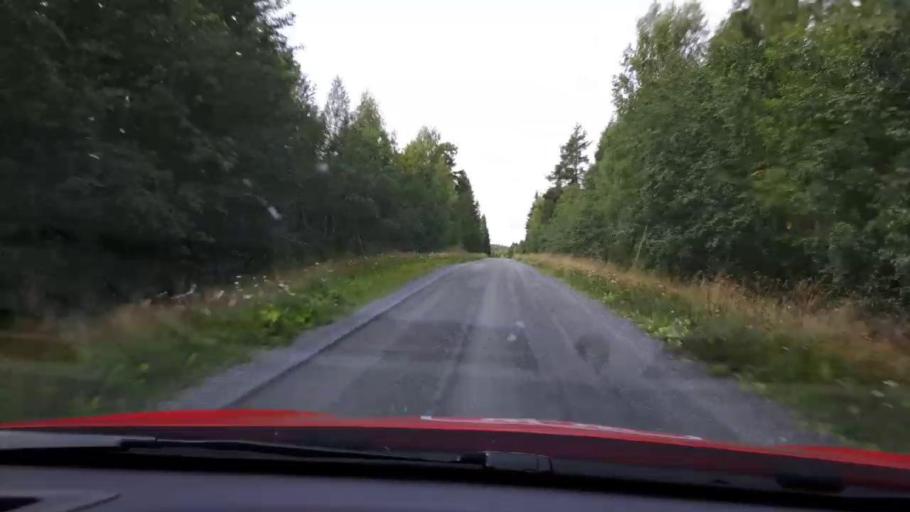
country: SE
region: Jaemtland
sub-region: Krokoms Kommun
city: Valla
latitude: 63.2670
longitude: 13.7784
